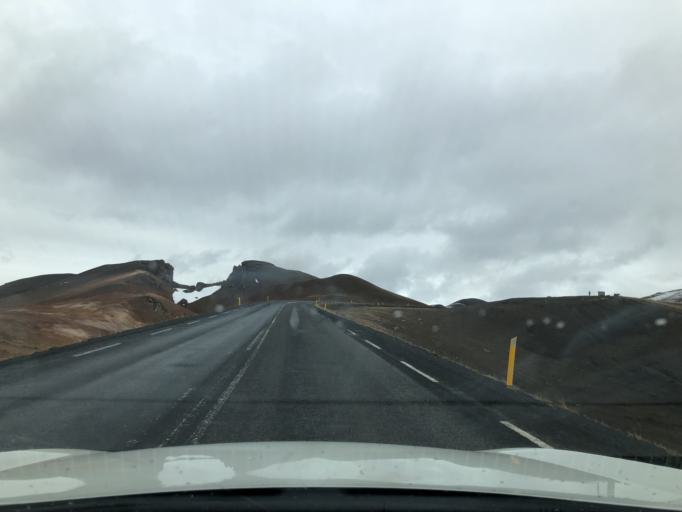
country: IS
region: Northeast
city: Laugar
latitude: 65.6408
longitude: -16.8373
